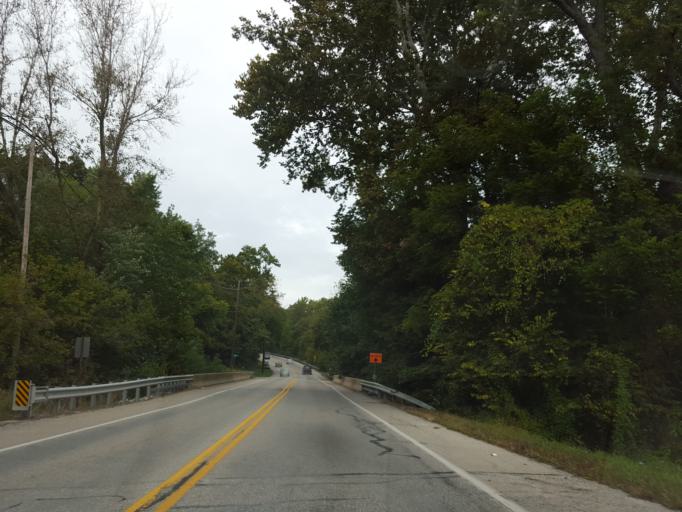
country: US
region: Pennsylvania
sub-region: York County
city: West York
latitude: 39.9214
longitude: -76.7982
